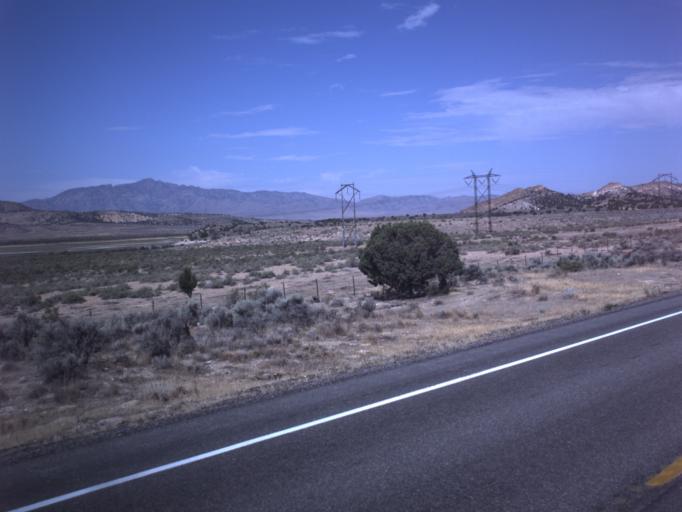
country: US
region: Utah
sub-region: Sanpete County
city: Gunnison
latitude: 39.3454
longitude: -111.9250
